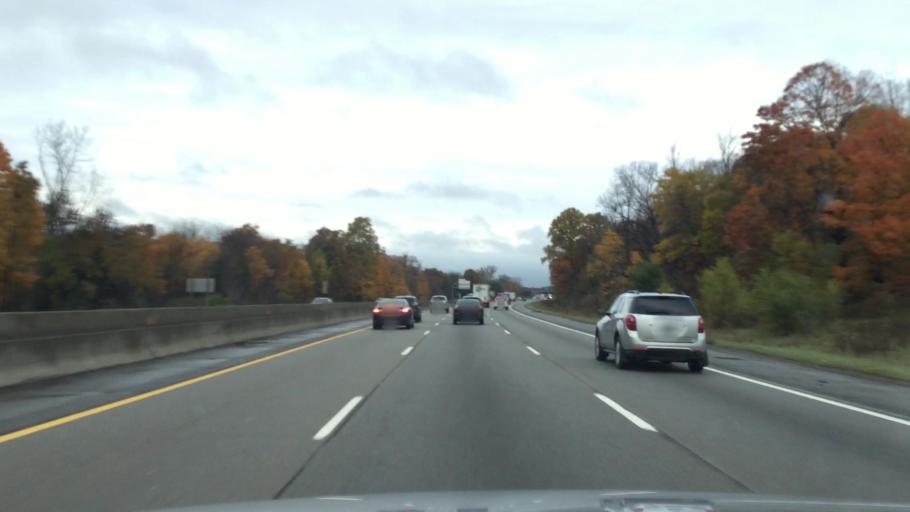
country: US
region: Michigan
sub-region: Washtenaw County
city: Ypsilanti
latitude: 42.2248
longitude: -83.6359
